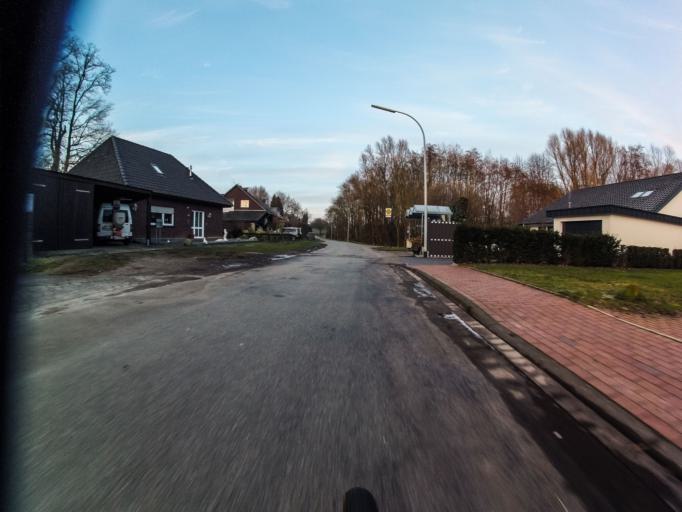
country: DE
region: North Rhine-Westphalia
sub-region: Regierungsbezirk Munster
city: Westerkappeln
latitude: 52.2683
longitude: 7.8520
